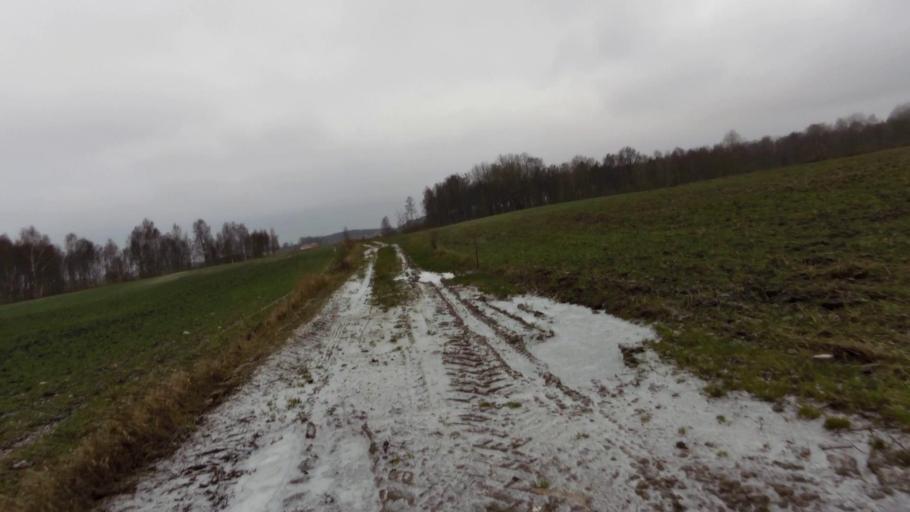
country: PL
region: West Pomeranian Voivodeship
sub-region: Powiat szczecinecki
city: Szczecinek
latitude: 53.6472
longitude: 16.6200
